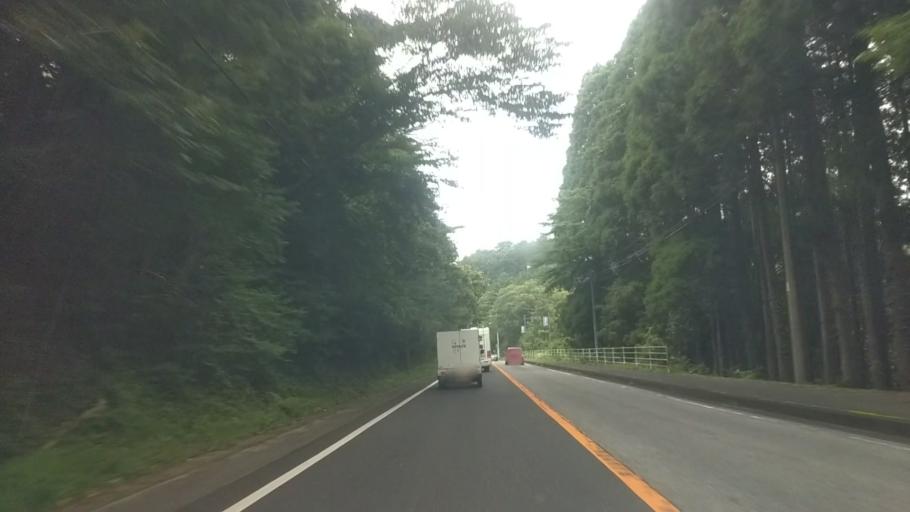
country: JP
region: Chiba
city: Kawaguchi
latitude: 35.1872
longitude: 140.0610
